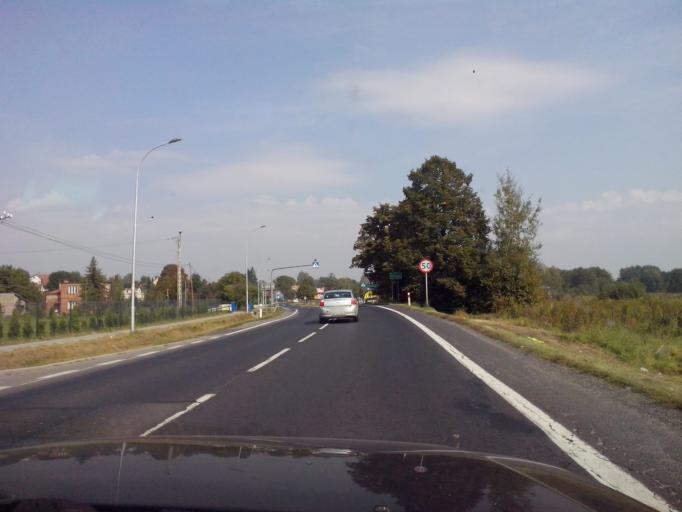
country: PL
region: Subcarpathian Voivodeship
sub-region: Powiat rzeszowski
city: Lutoryz
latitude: 49.9568
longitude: 21.9164
